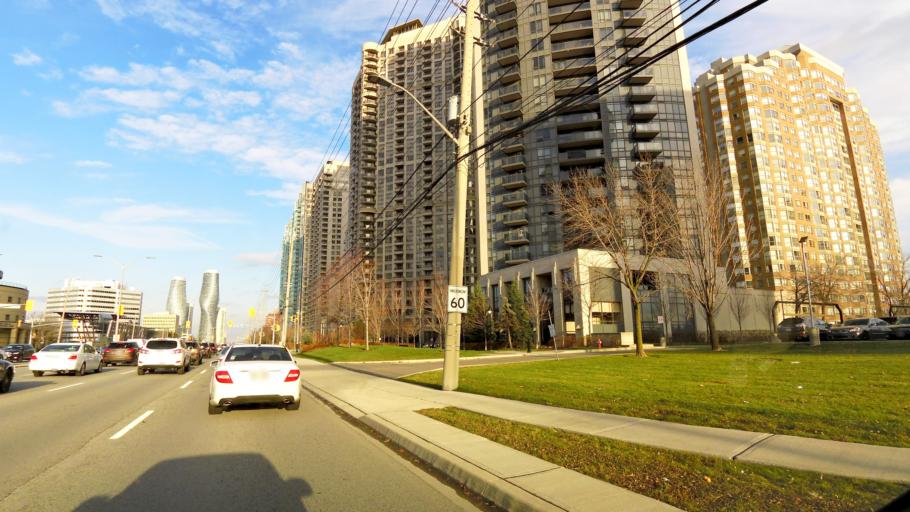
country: CA
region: Ontario
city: Mississauga
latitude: 43.5861
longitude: -79.6439
